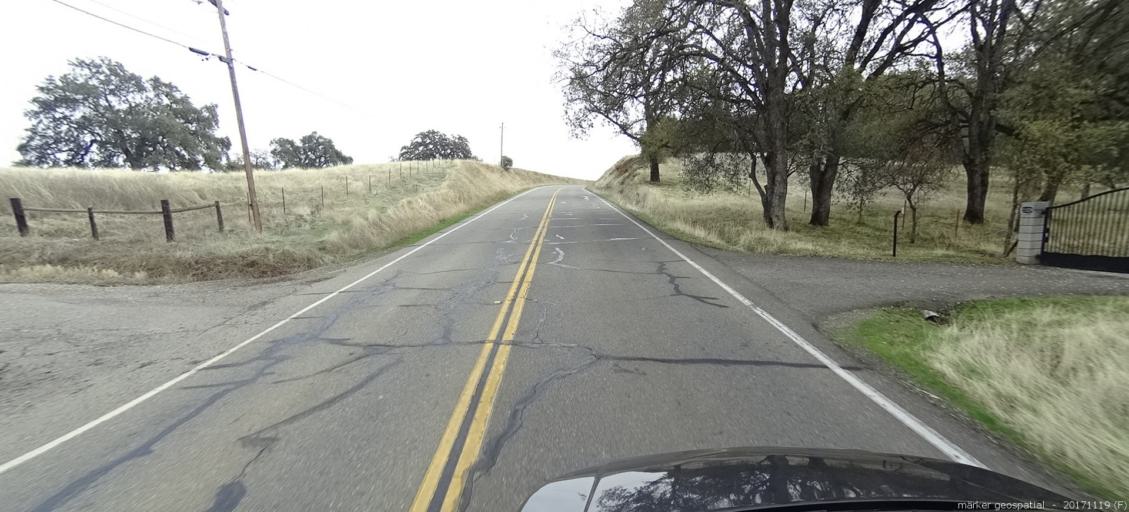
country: US
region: California
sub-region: Shasta County
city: Anderson
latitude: 40.4794
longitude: -122.2554
